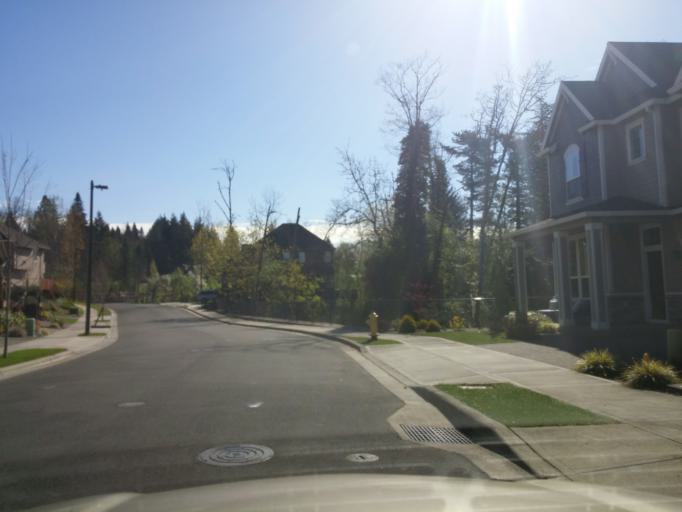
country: US
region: Oregon
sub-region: Washington County
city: Cedar Mill
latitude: 45.5387
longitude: -122.7946
